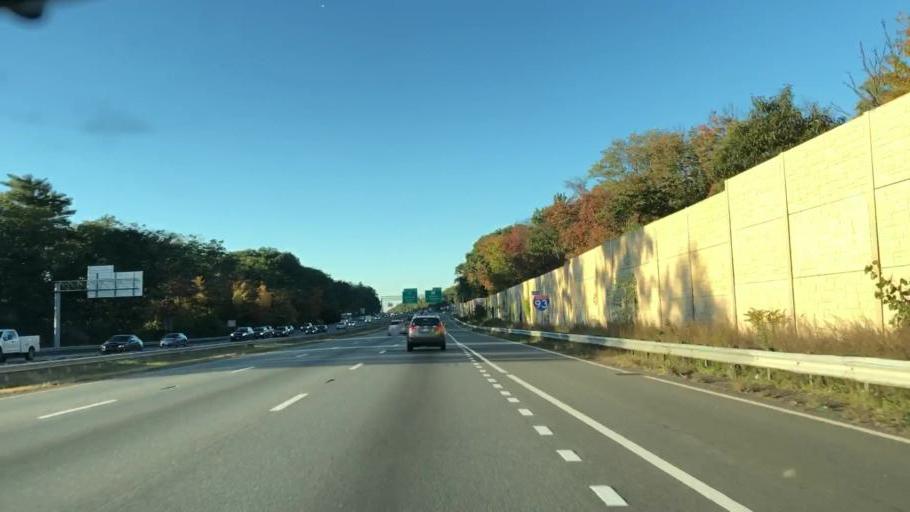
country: US
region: Massachusetts
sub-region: Essex County
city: Andover
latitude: 42.6275
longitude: -71.1784
